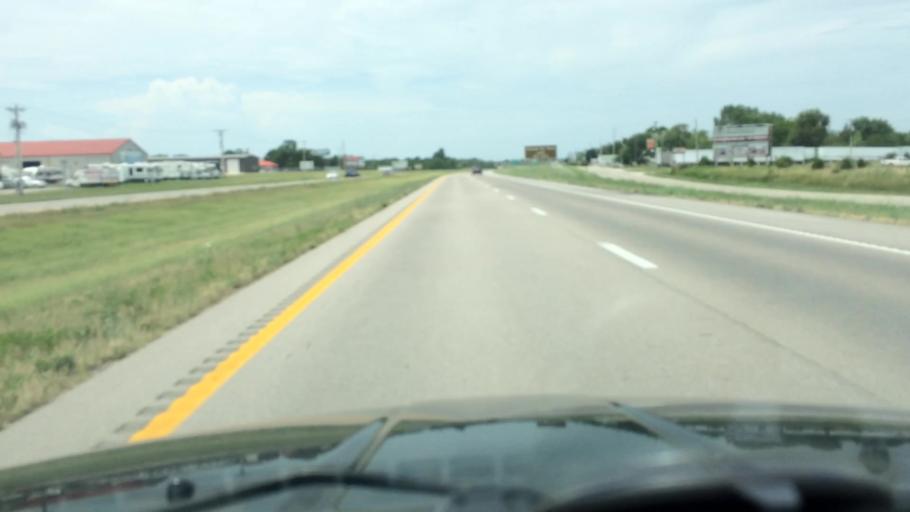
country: US
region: Missouri
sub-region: Polk County
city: Bolivar
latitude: 37.5615
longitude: -93.3919
